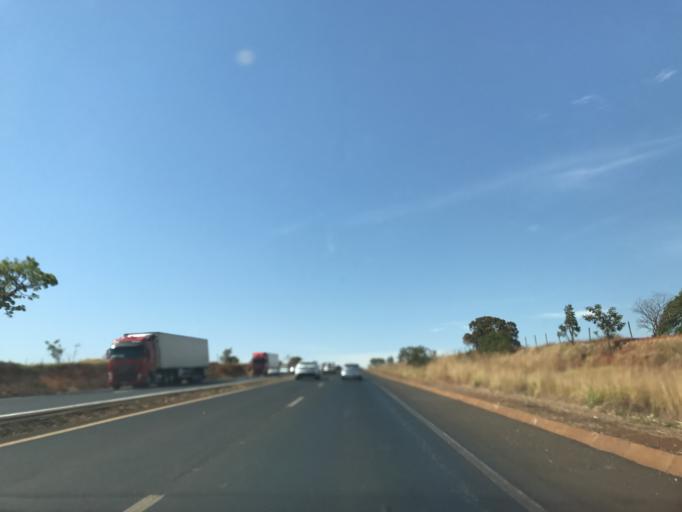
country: BR
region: Minas Gerais
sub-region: Centralina
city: Centralina
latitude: -18.6639
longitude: -49.1651
